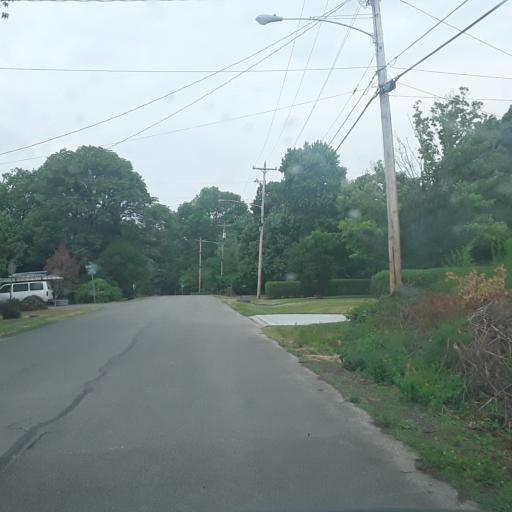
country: US
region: Tennessee
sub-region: Davidson County
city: Oak Hill
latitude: 36.0735
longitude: -86.7567
